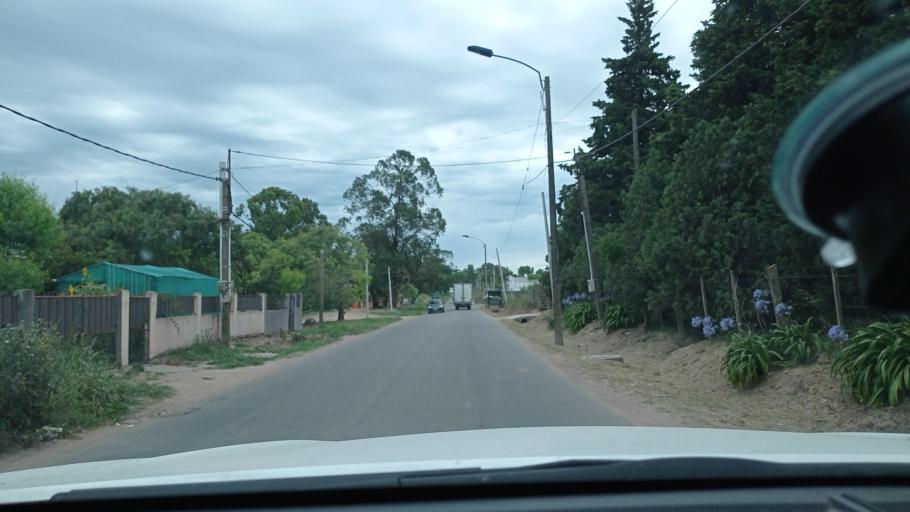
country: UY
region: Canelones
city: La Paz
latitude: -34.8156
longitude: -56.1955
